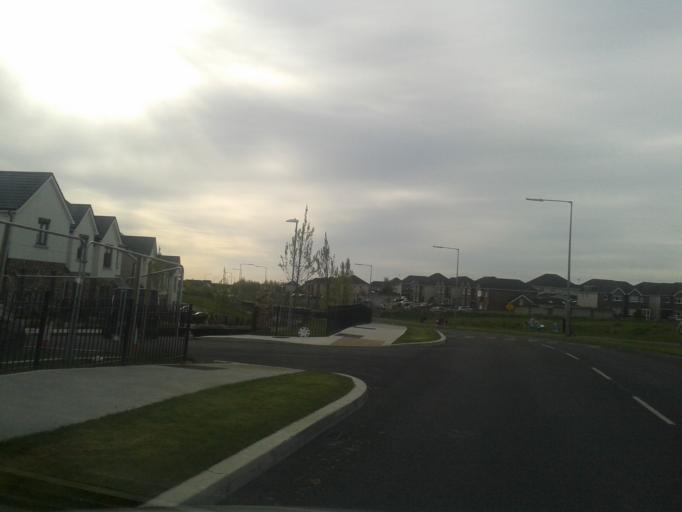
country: IE
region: Leinster
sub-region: Fingal County
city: Swords
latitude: 53.4718
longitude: -6.2430
